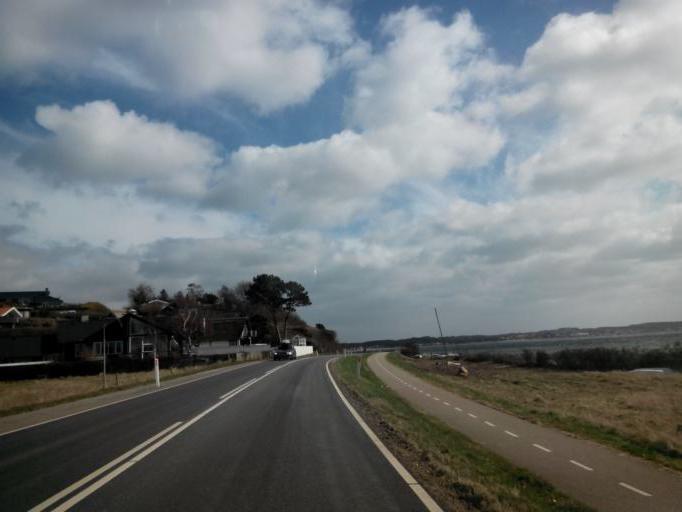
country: DK
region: Central Jutland
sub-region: Syddjurs Kommune
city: Ebeltoft
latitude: 56.2267
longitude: 10.6447
